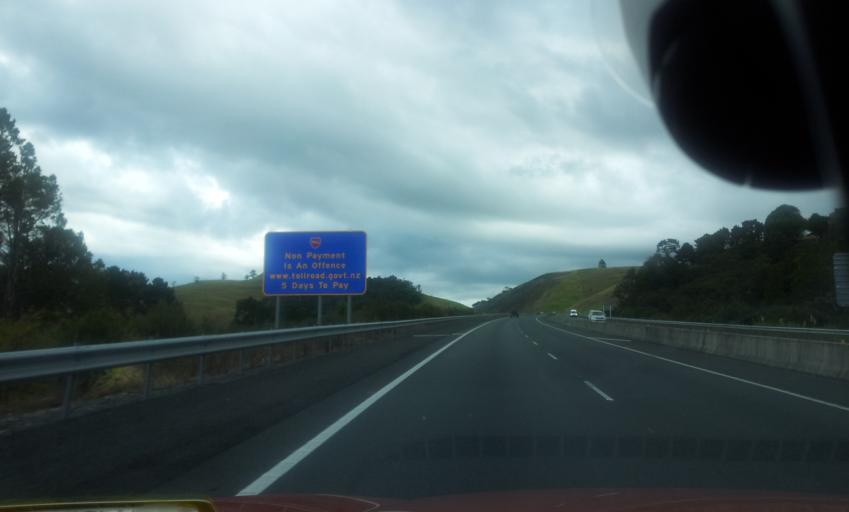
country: NZ
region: Auckland
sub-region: Auckland
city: Warkworth
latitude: -36.5451
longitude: 174.6811
